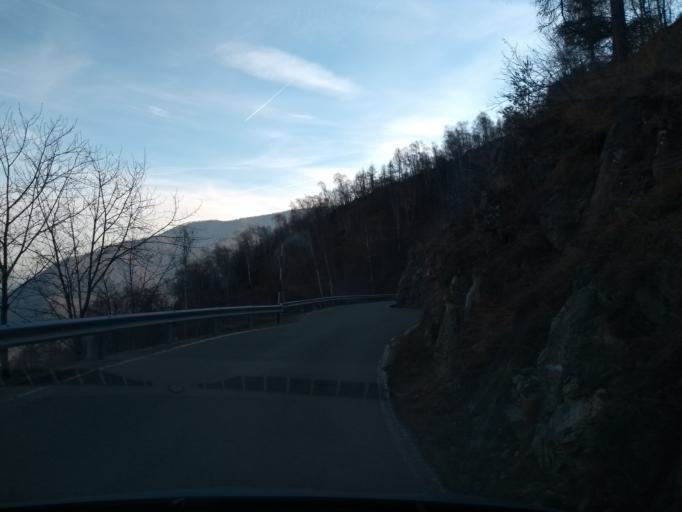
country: IT
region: Piedmont
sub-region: Provincia di Torino
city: Coassolo Torinese
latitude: 45.2791
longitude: 7.4572
